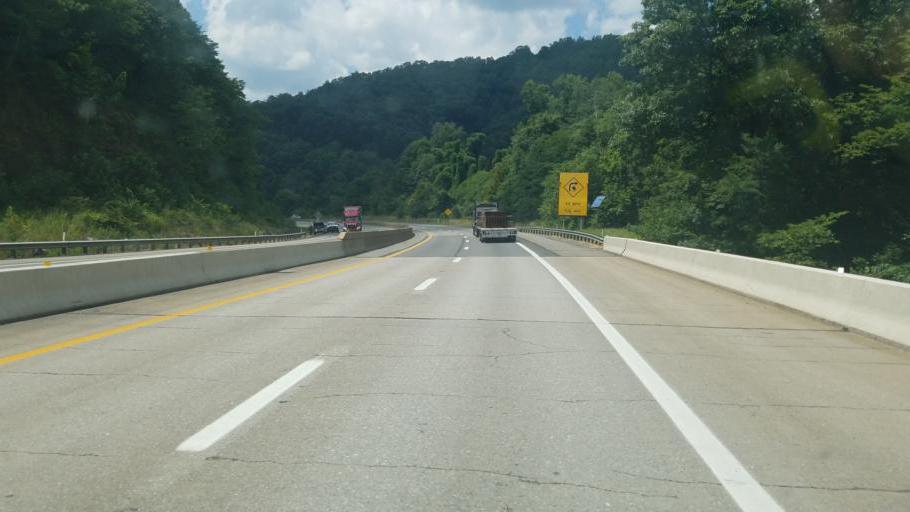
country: US
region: West Virginia
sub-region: Kanawha County
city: Montgomery
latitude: 37.9962
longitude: -81.3387
